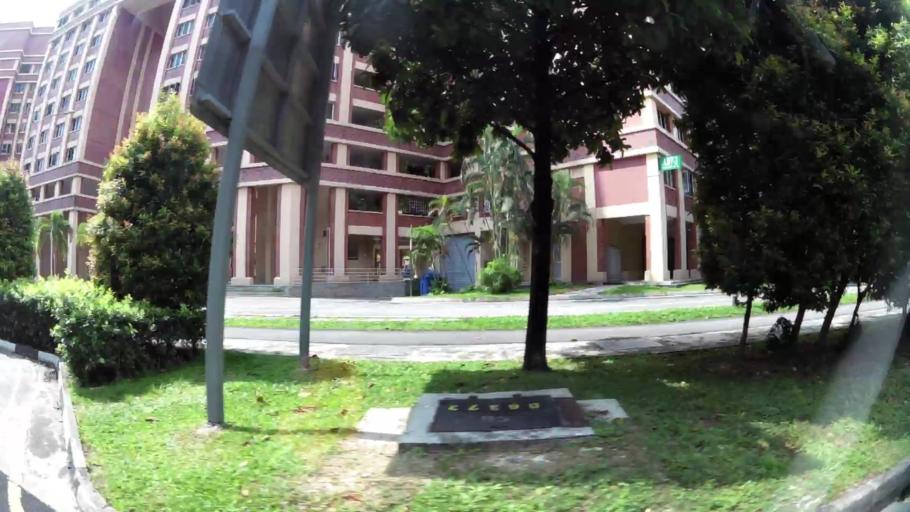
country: SG
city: Singapore
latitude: 1.3590
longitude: 103.9598
